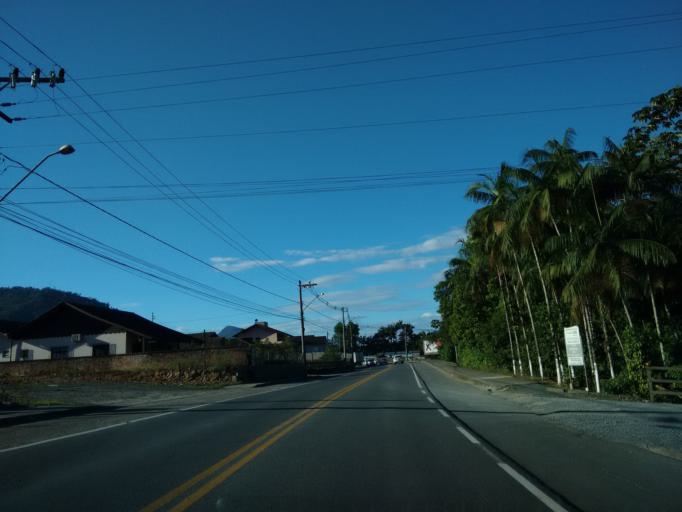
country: BR
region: Santa Catarina
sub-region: Pomerode
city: Pomerode
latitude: -26.7585
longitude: -49.1714
